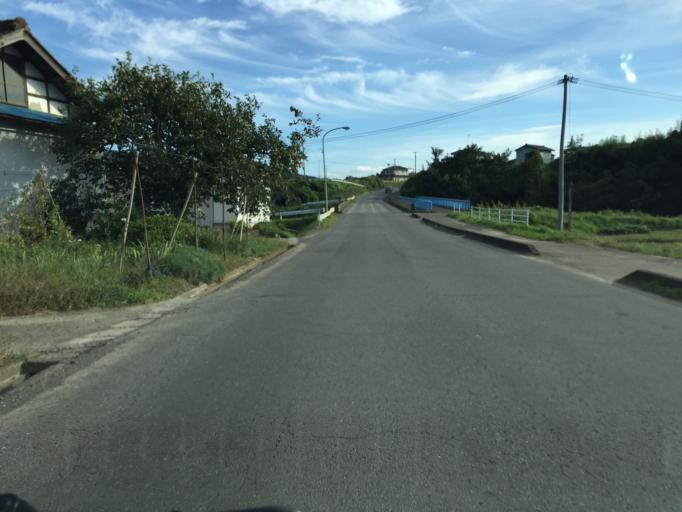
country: JP
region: Fukushima
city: Yanagawamachi-saiwaicho
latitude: 37.8486
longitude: 140.6151
